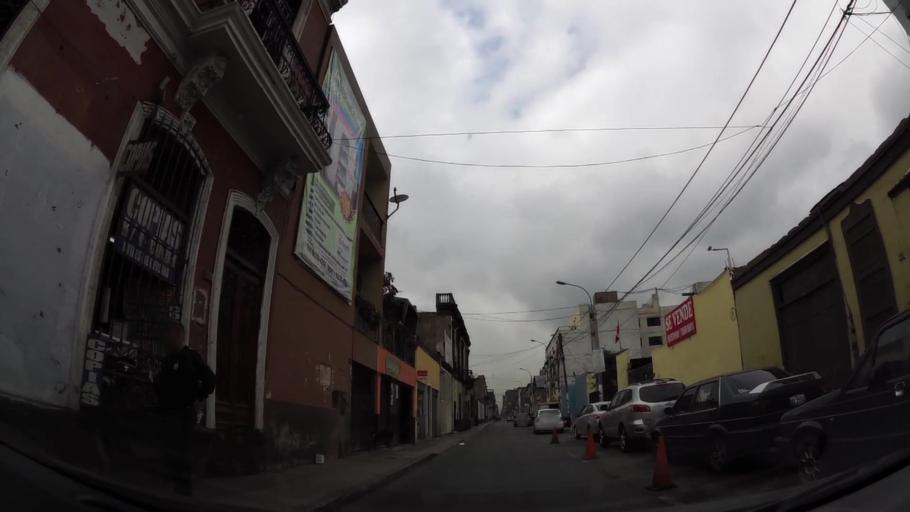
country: PE
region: Lima
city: Lima
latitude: -12.0412
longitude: -77.0391
